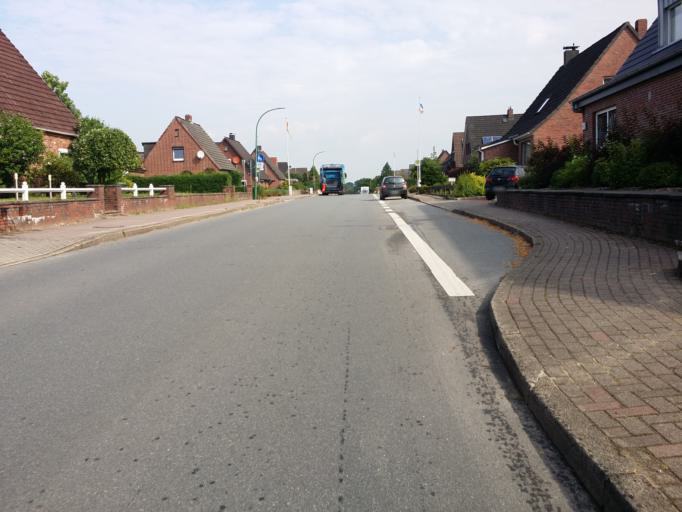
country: DE
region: Schleswig-Holstein
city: Oldendorf
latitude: 53.9493
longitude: 9.4629
